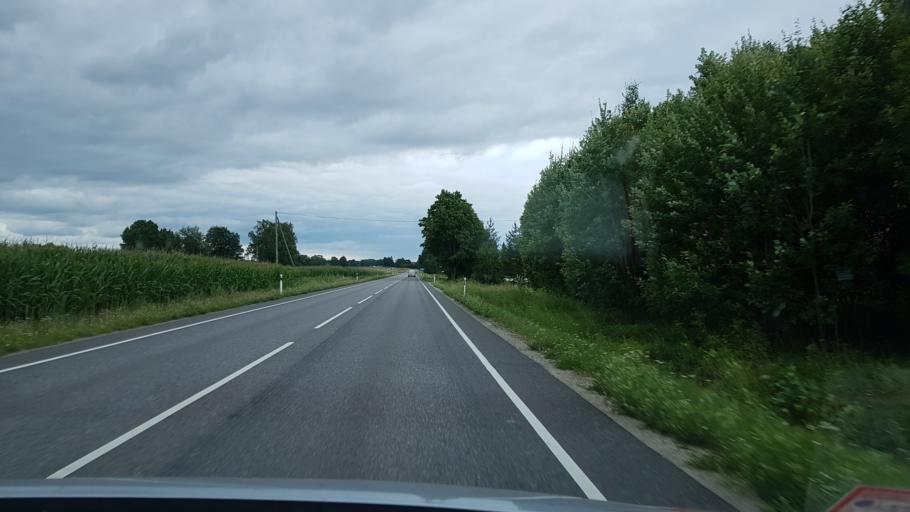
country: EE
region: Tartu
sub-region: Tartu linn
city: Tartu
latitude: 58.4257
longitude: 26.8549
